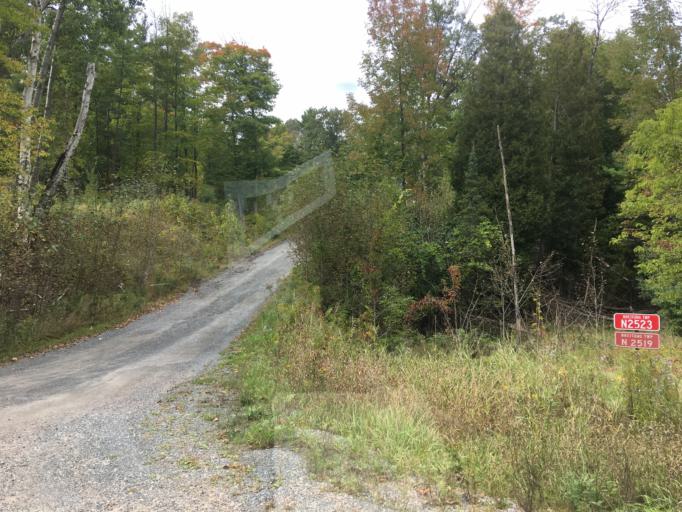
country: US
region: Michigan
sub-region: Dickinson County
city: Quinnesec
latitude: 45.8093
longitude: -87.9881
